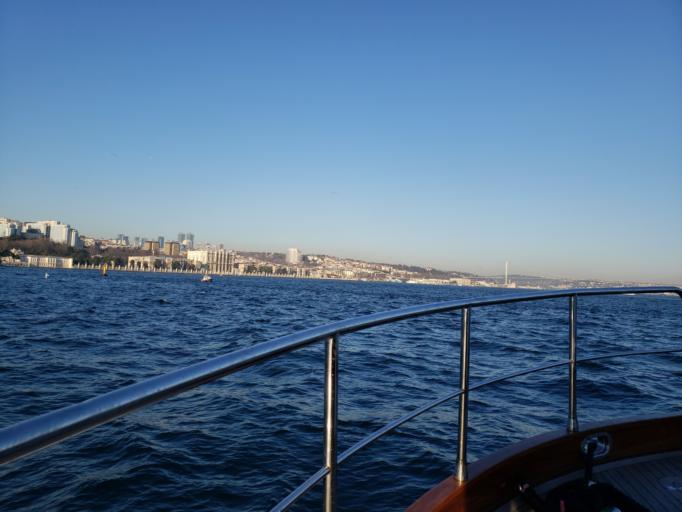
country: TR
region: Istanbul
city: Eminoenue
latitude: 41.0319
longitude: 28.9961
